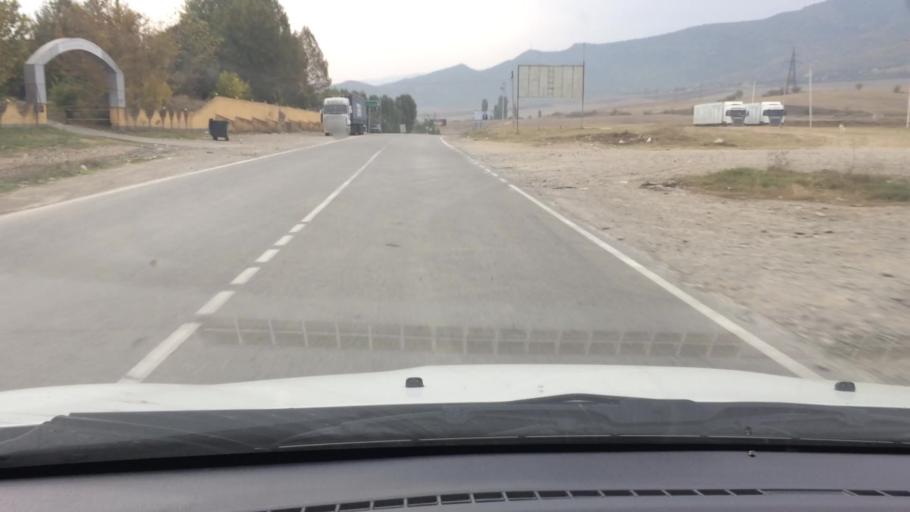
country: AM
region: Tavush
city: Bagratashen
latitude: 41.2324
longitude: 44.8166
